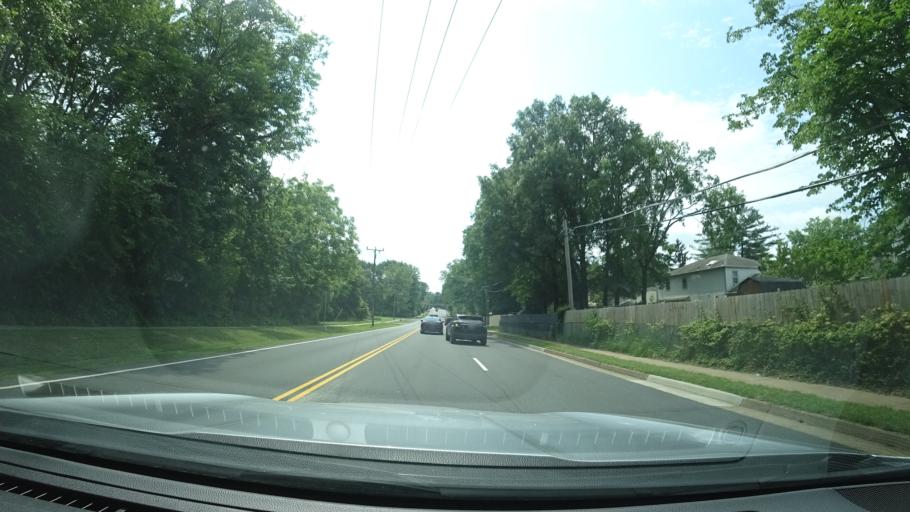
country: US
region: Virginia
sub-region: Fairfax County
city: Herndon
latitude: 38.9708
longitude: -77.3984
